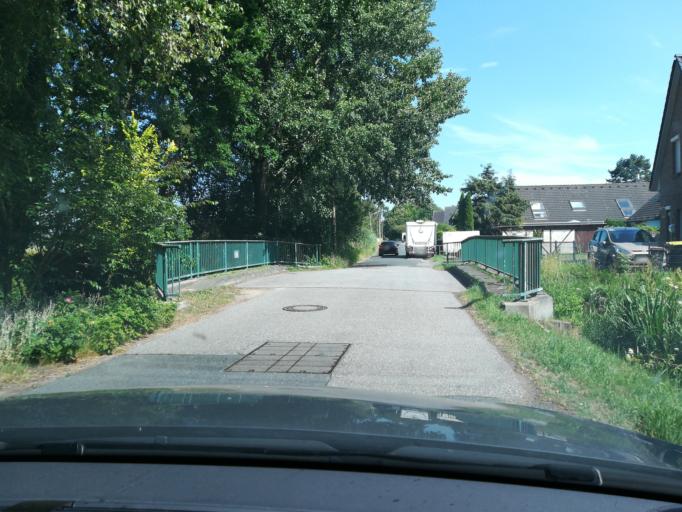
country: DE
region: Hamburg
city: Rothenburgsort
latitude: 53.4943
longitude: 10.0232
